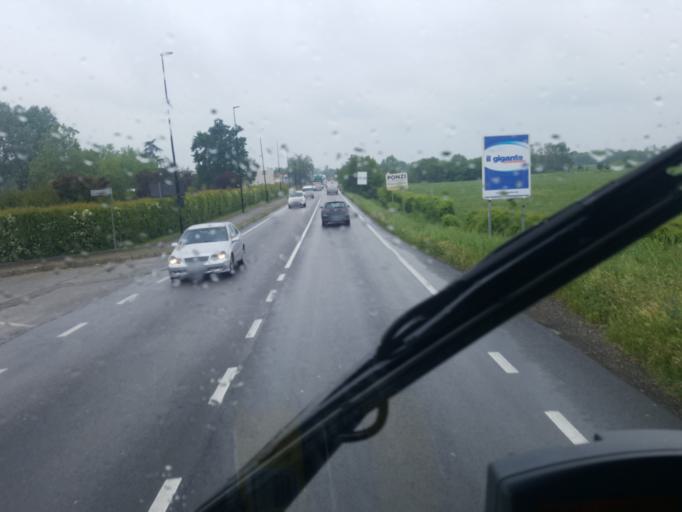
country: IT
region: Emilia-Romagna
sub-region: Provincia di Reggio Emilia
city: Roncocesi
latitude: 44.7202
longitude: 10.5690
